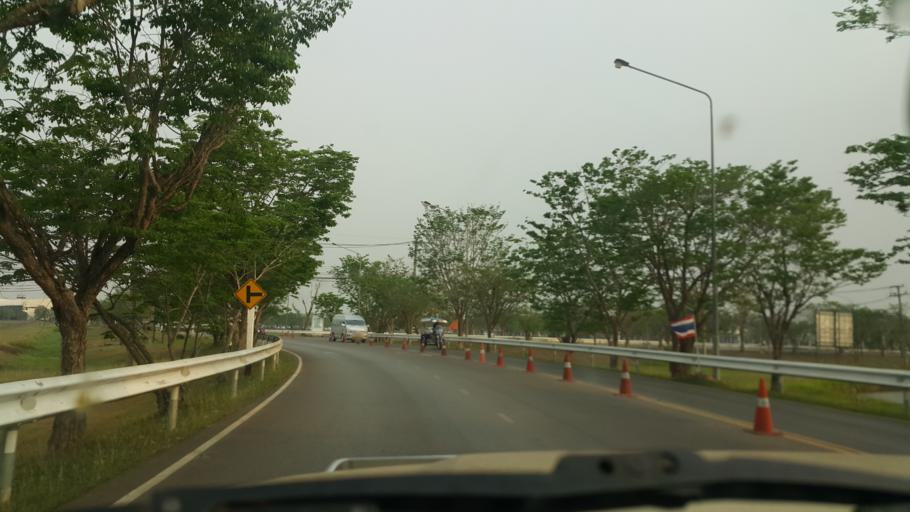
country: TH
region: Changwat Udon Thani
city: Udon Thani
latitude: 17.3891
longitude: 102.7706
